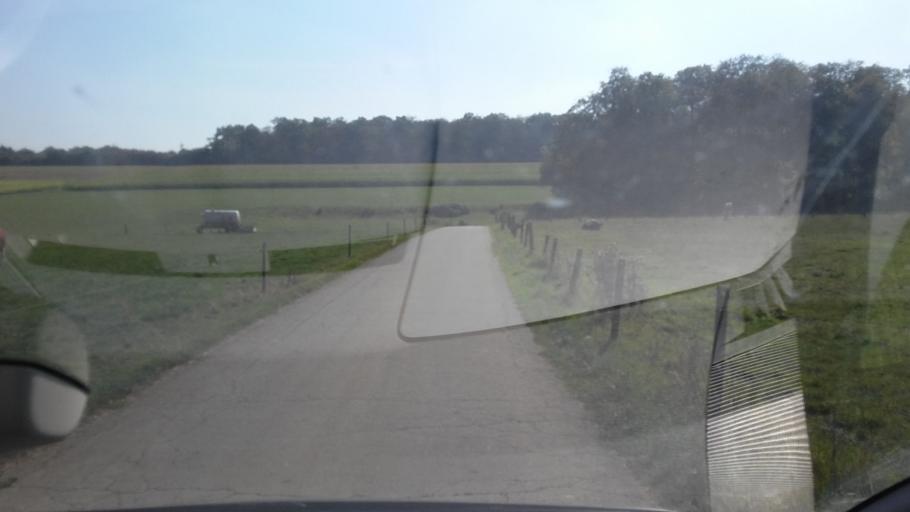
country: LU
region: Luxembourg
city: Eischen
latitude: 49.7095
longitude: 5.8653
